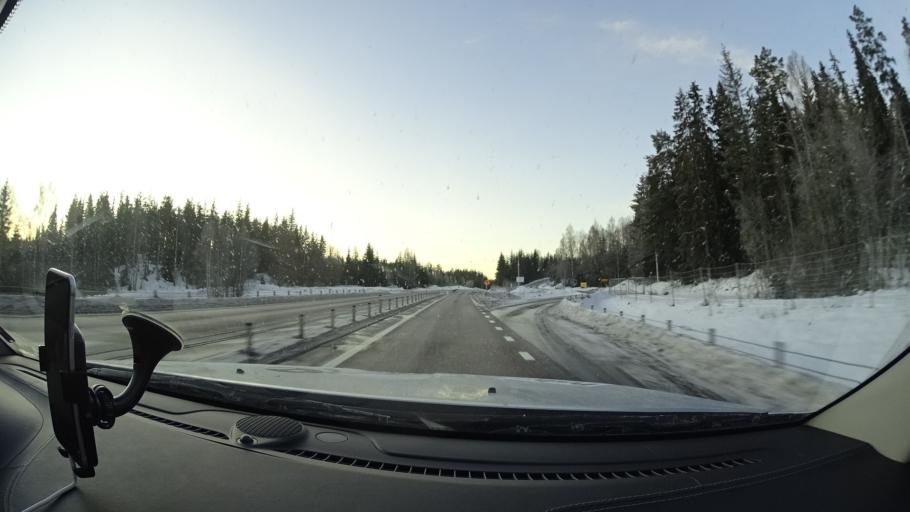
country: SE
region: Dalarna
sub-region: Borlange Kommun
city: Borlaenge
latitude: 60.4476
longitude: 15.3686
